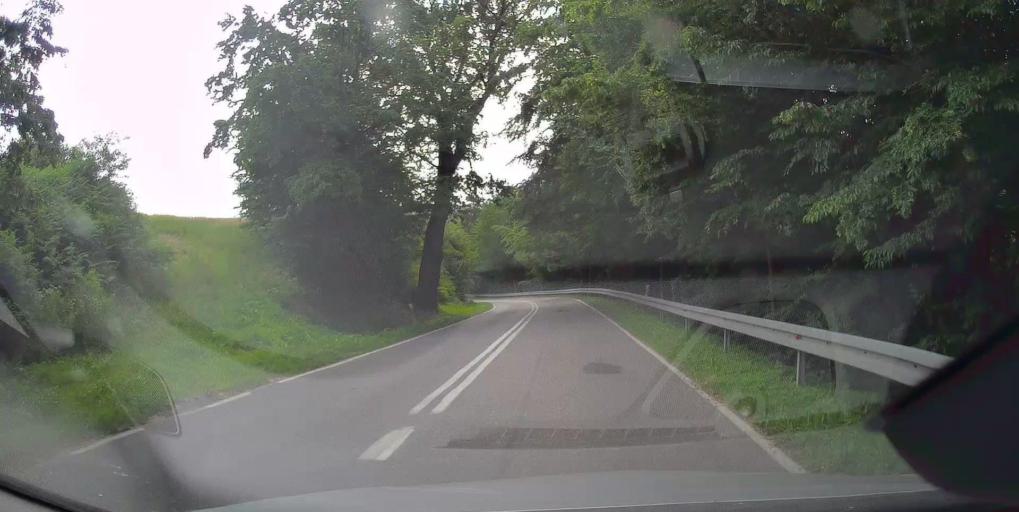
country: PL
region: Lesser Poland Voivodeship
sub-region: Powiat tarnowski
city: Zakliczyn
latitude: 49.7651
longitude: 20.7814
